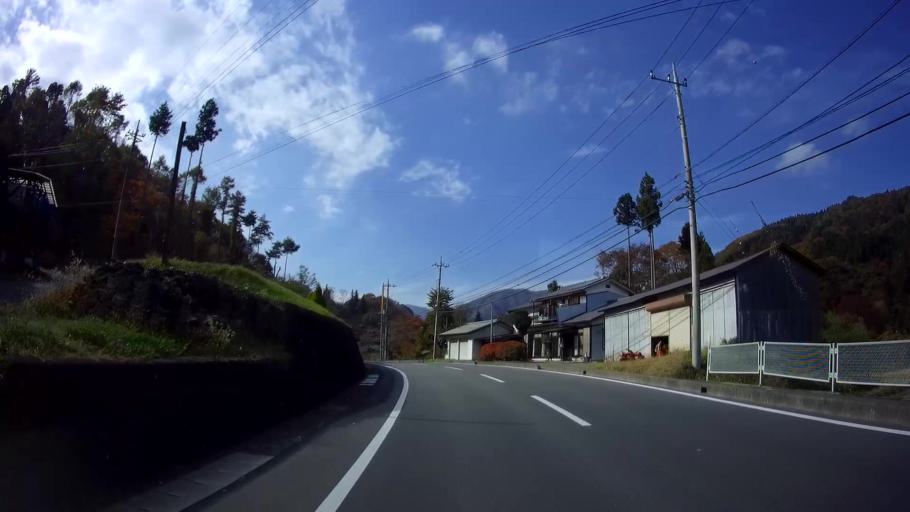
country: JP
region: Gunma
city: Nakanojomachi
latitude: 36.5053
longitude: 138.7244
